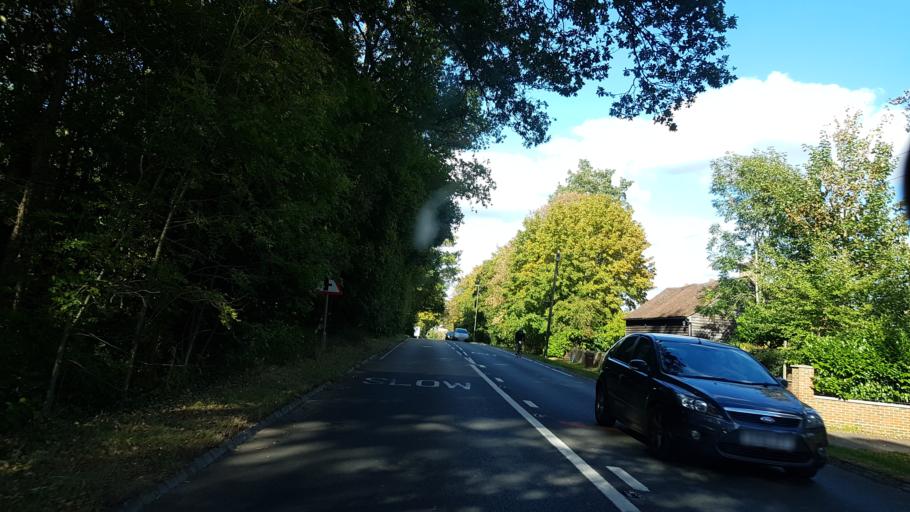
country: GB
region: England
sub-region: Surrey
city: Milford
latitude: 51.1656
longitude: -0.6495
